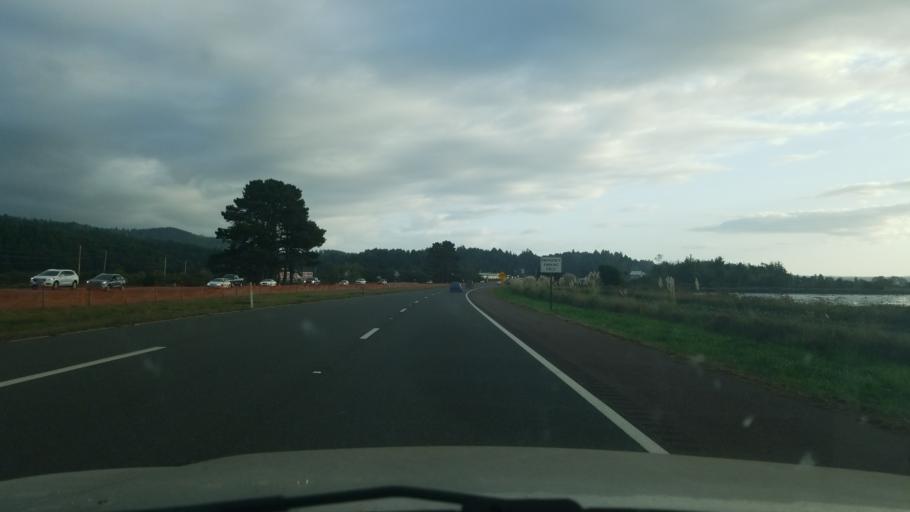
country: US
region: California
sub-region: Humboldt County
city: Bayside
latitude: 40.8342
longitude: -124.0823
